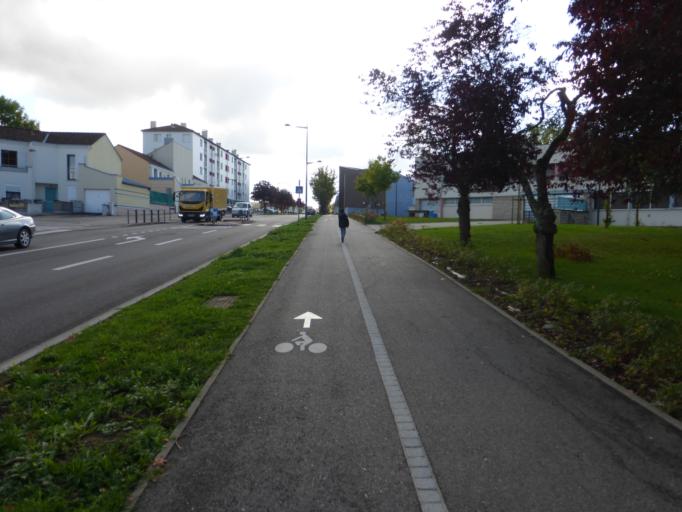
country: FR
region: Lorraine
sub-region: Departement de Meurthe-et-Moselle
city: Villers-les-Nancy
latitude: 48.6714
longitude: 6.1616
